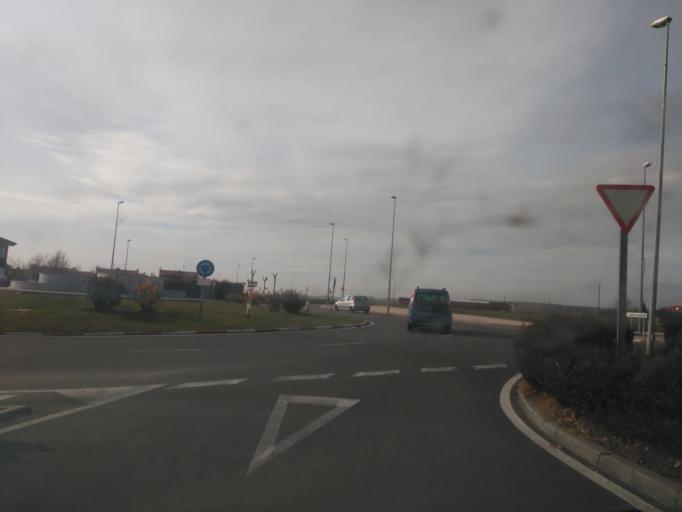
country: ES
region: Castille and Leon
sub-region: Provincia de Salamanca
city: Cabrerizos
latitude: 40.9802
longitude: -5.6107
